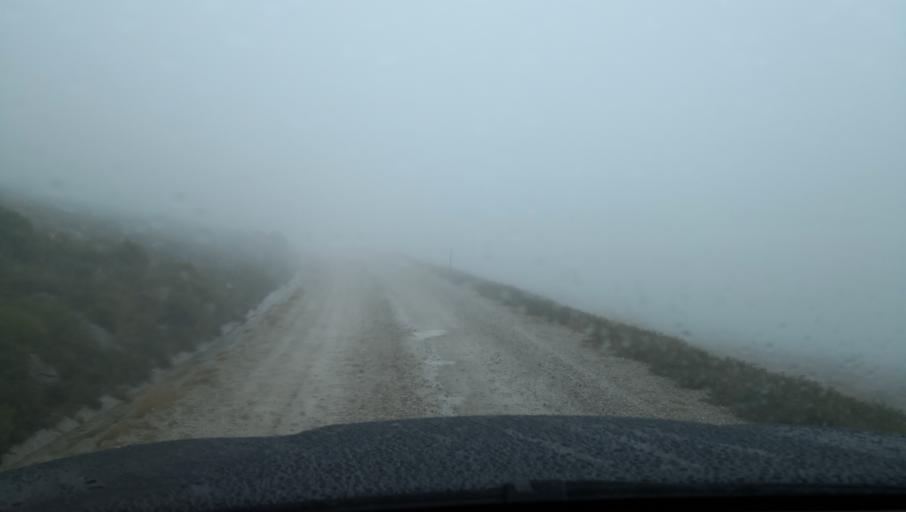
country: PT
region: Vila Real
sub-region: Vila Real
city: Vila Real
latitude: 41.3347
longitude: -7.8396
